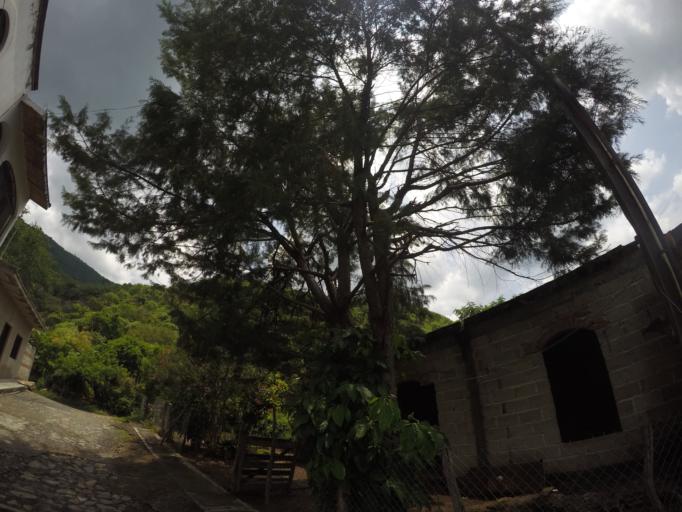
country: MX
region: Nayarit
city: Jala
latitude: 21.1035
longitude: -104.4366
